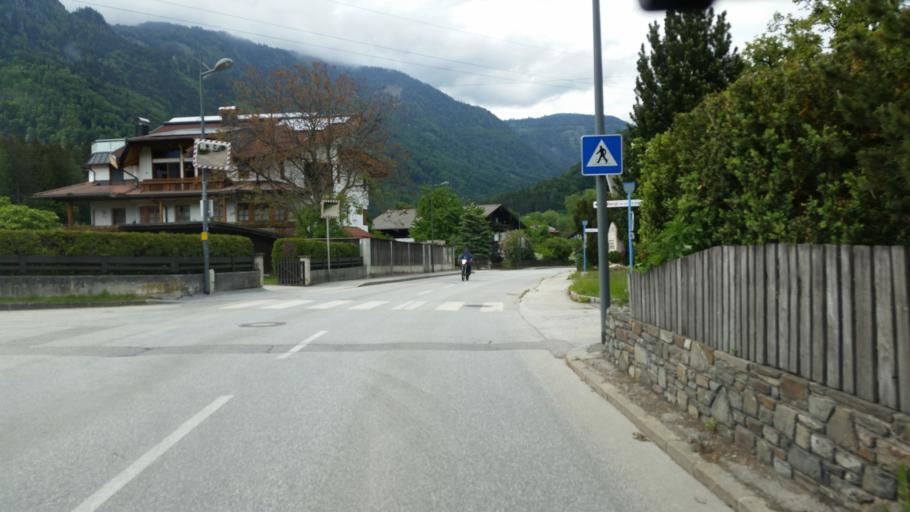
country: AT
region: Tyrol
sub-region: Politischer Bezirk Kufstein
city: Kramsach
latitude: 47.4441
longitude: 11.8757
